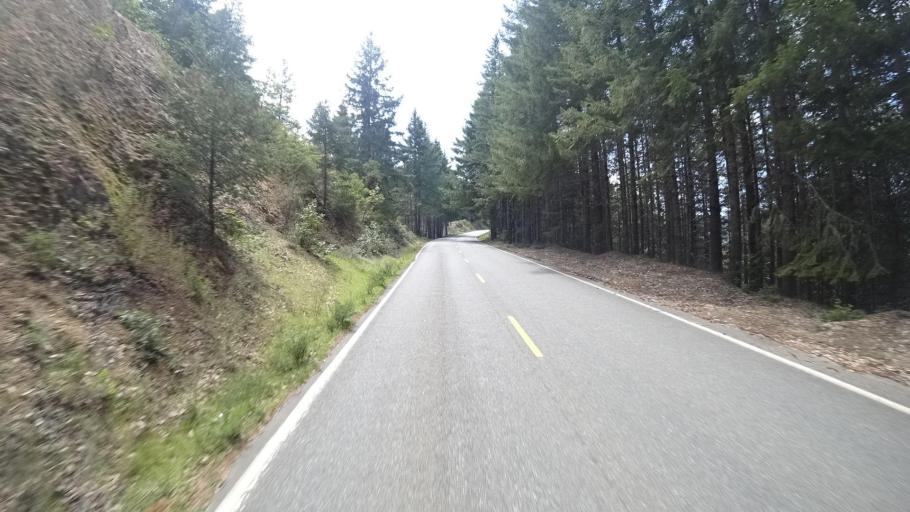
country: US
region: California
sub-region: Humboldt County
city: Redway
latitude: 40.0531
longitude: -124.0022
